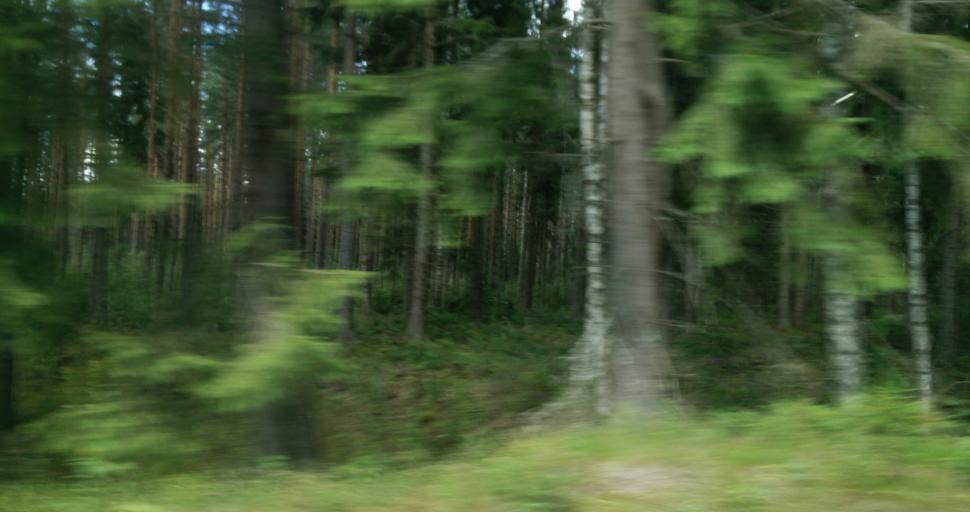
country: SE
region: Vaermland
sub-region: Hagfors Kommun
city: Hagfors
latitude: 60.0371
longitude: 13.5385
